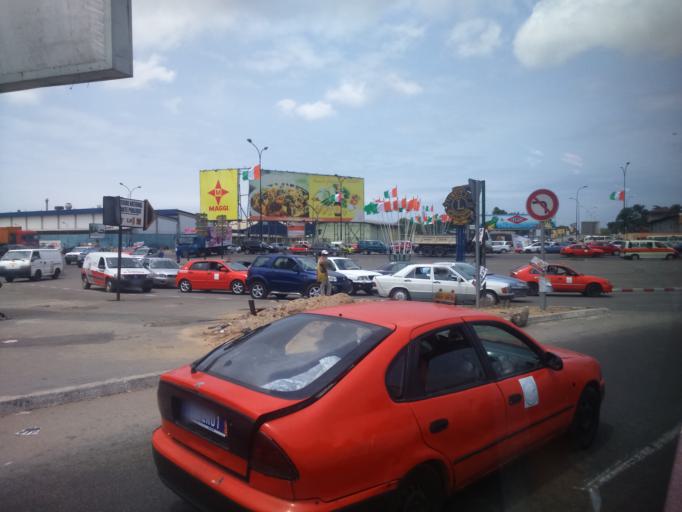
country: CI
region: Lagunes
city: Abidjan
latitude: 5.3018
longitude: -3.9941
